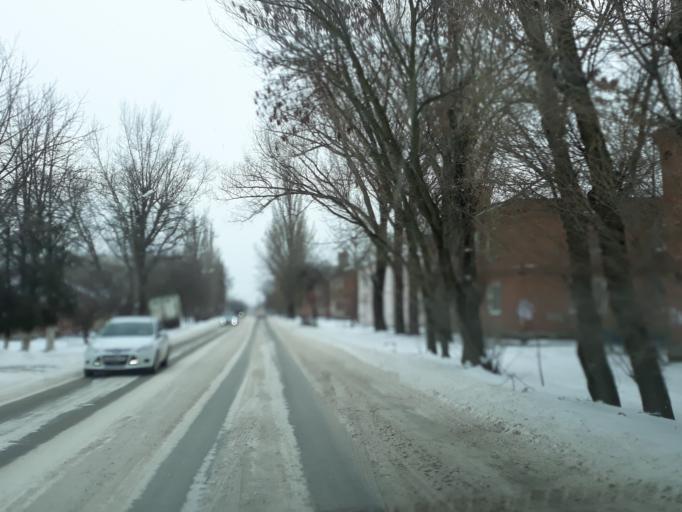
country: RU
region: Rostov
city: Taganrog
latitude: 47.2360
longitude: 38.8767
